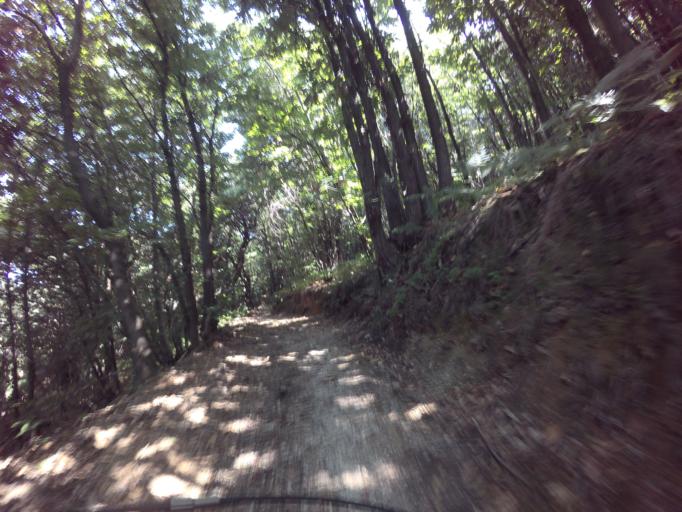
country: IT
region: Piedmont
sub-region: Provincia di Cuneo
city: Roccaforte Mondovi
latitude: 44.3272
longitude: 7.7127
